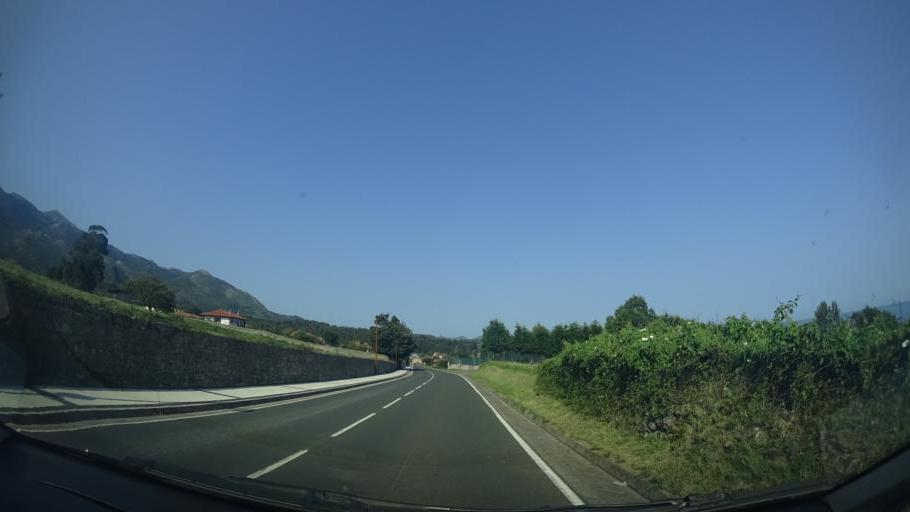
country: ES
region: Asturias
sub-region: Province of Asturias
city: Colunga
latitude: 43.4674
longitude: -5.2030
